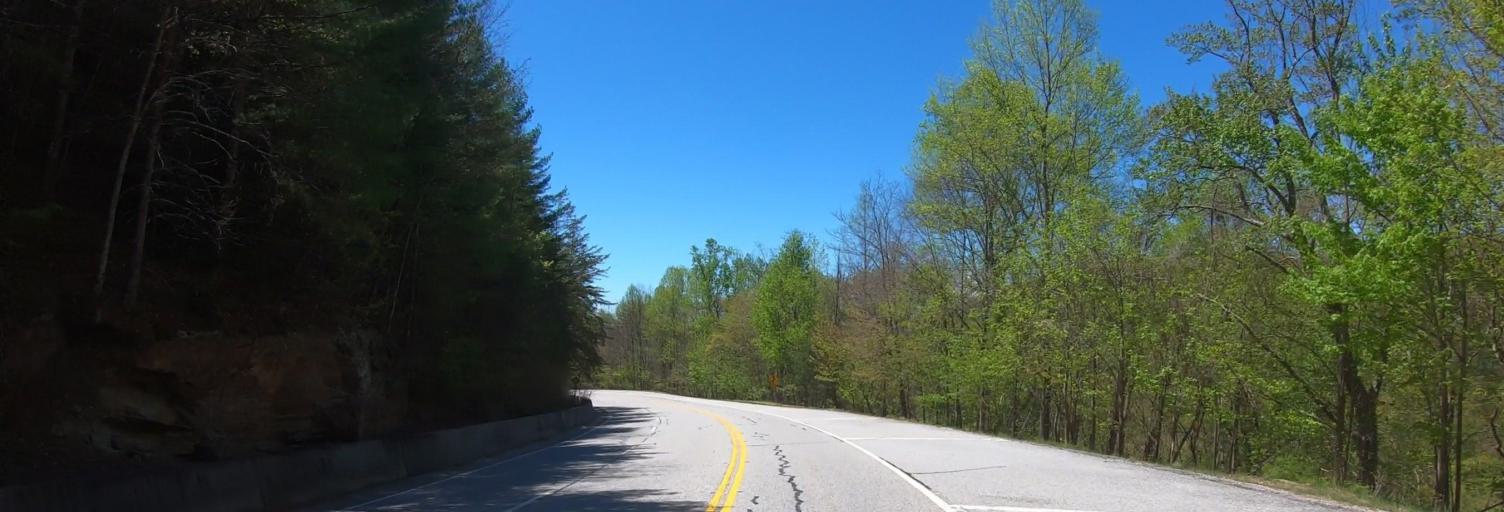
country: US
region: Georgia
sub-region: Towns County
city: Hiawassee
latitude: 34.7912
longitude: -83.7431
